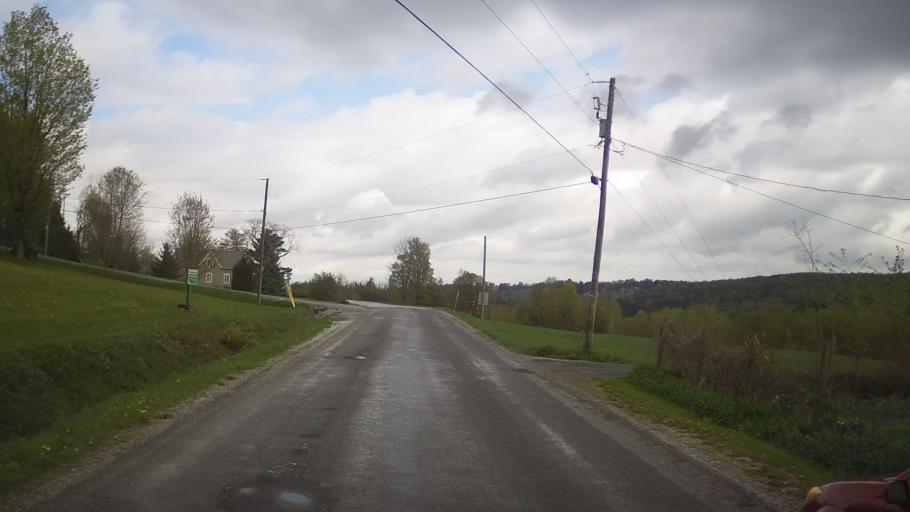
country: CA
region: Quebec
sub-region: Monteregie
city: Cowansville
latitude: 45.1952
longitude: -72.7039
